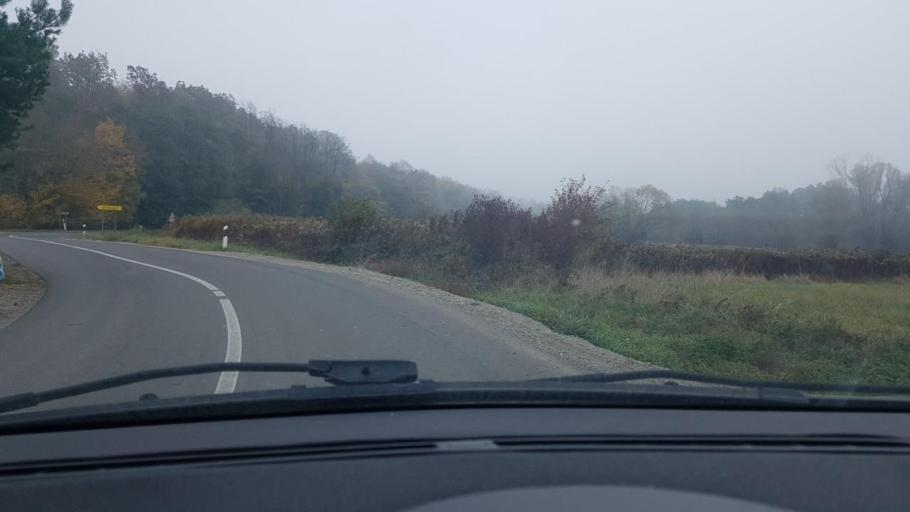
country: HR
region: Varazdinska
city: Ivanec
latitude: 46.1378
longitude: 16.1741
